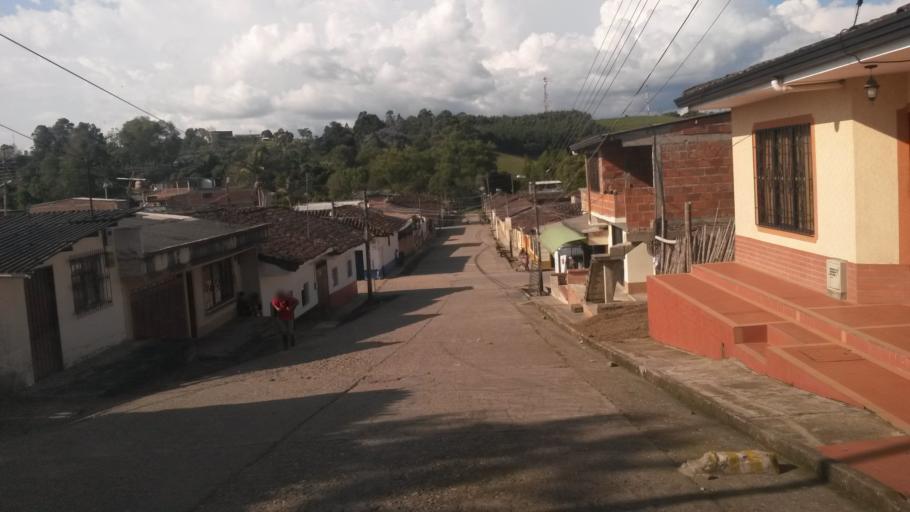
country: CO
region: Cauca
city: Rosas
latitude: 2.3520
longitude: -76.6823
